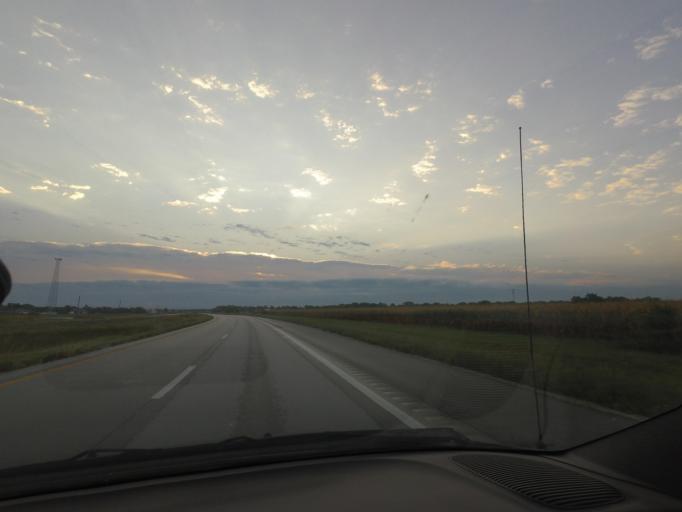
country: US
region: Missouri
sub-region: Macon County
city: Macon
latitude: 39.7502
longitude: -92.2738
